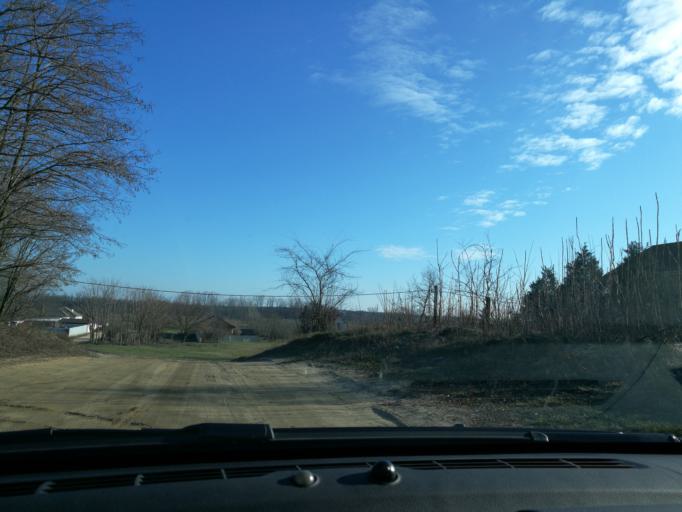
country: HU
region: Szabolcs-Szatmar-Bereg
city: Nyiregyhaza
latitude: 47.9244
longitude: 21.7585
